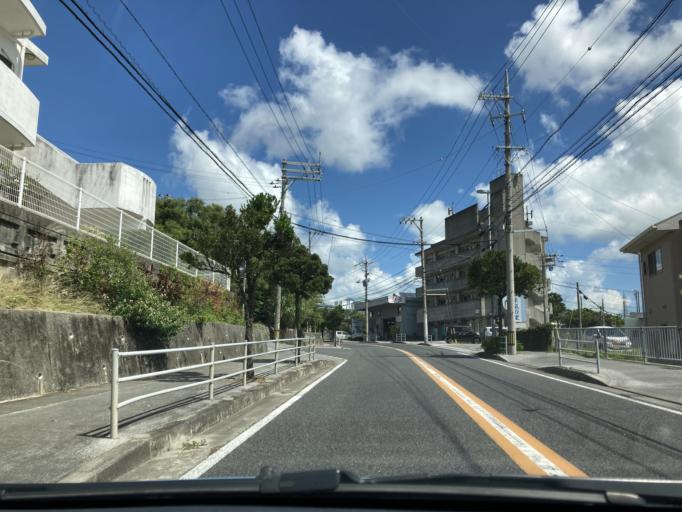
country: JP
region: Okinawa
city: Tomigusuku
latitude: 26.1694
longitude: 127.7209
